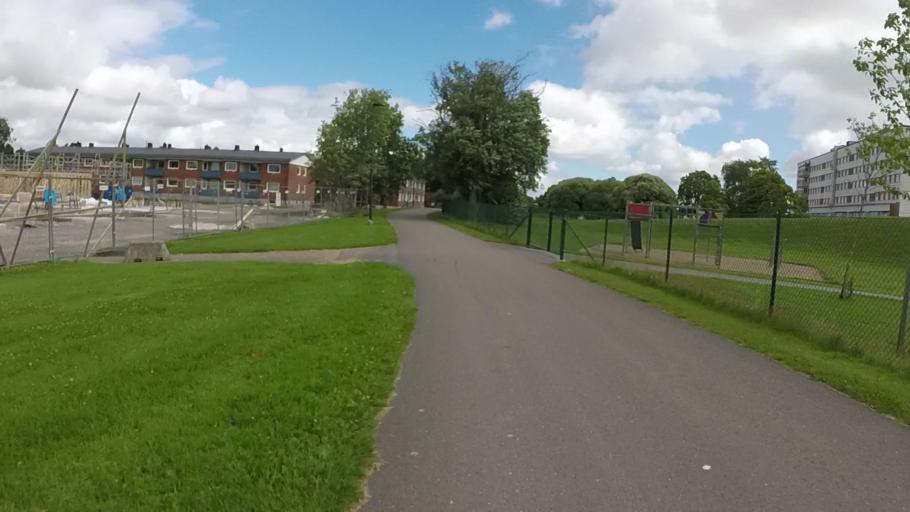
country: SE
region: Vaestra Goetaland
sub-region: Trollhattan
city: Trollhattan
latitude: 58.2696
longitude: 12.3041
